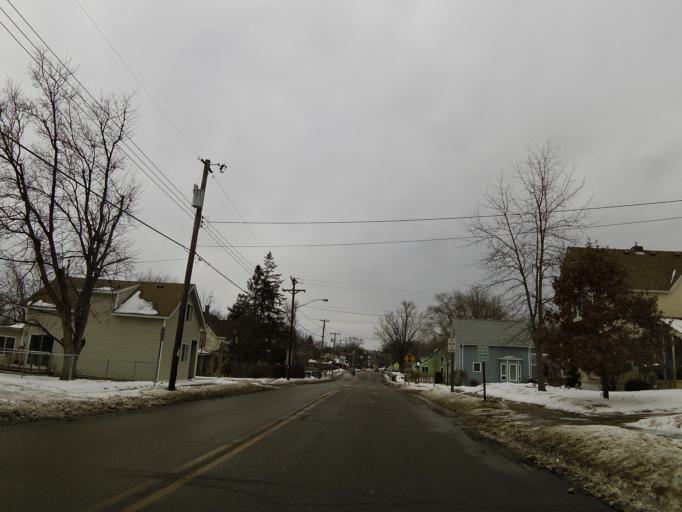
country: US
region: Wisconsin
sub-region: Saint Croix County
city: North Hudson
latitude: 44.9925
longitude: -92.7571
